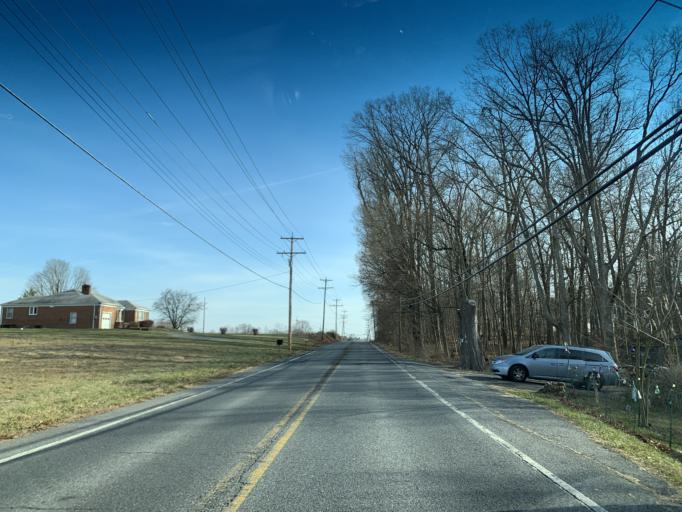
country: US
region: Maryland
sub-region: Carroll County
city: Eldersburg
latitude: 39.4252
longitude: -77.0005
